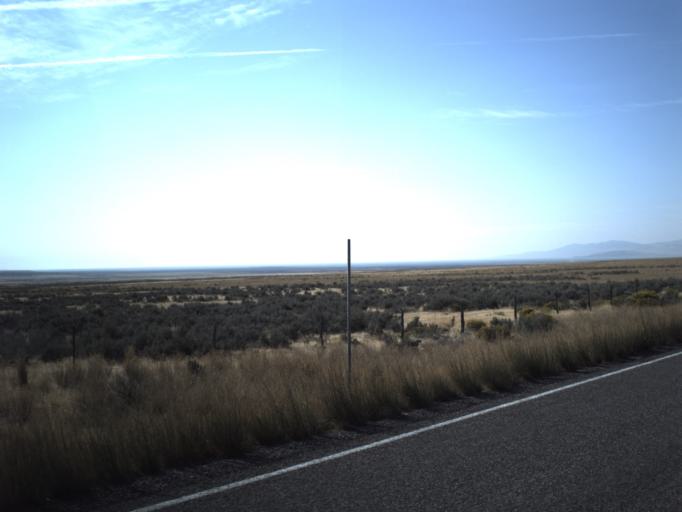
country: US
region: Idaho
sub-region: Oneida County
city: Malad City
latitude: 41.8927
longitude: -113.1109
